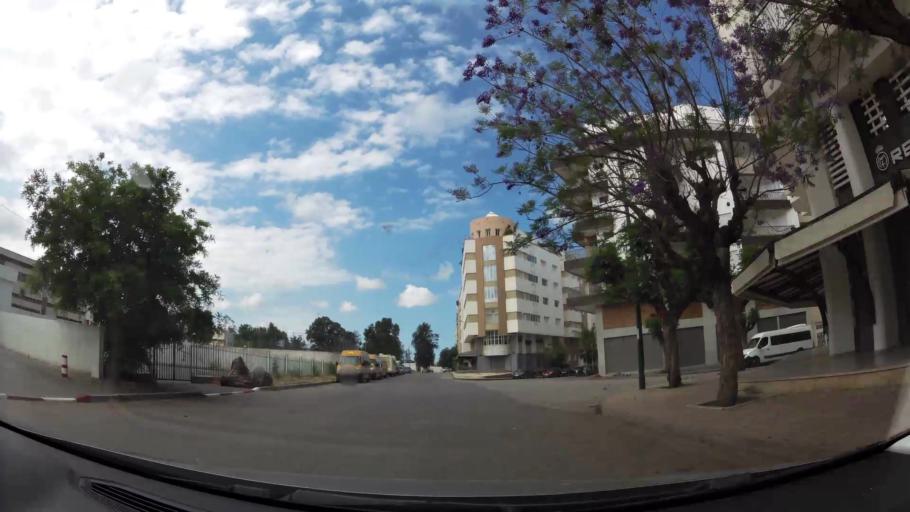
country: MA
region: Gharb-Chrarda-Beni Hssen
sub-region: Kenitra Province
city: Kenitra
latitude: 34.2529
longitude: -6.5910
